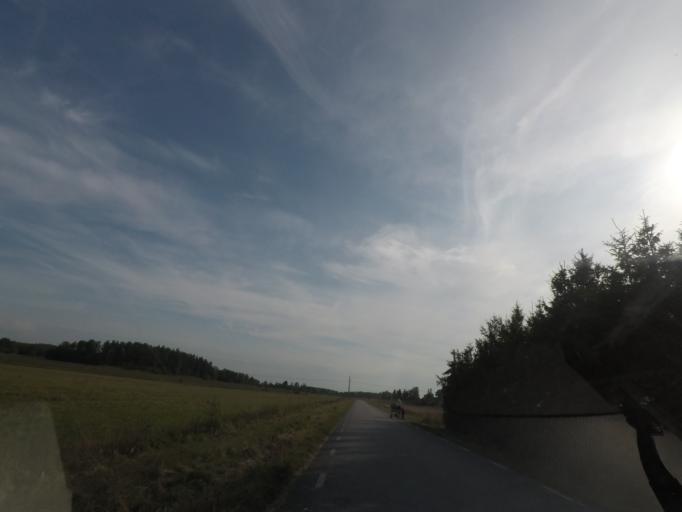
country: SE
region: Vaestmanland
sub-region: Hallstahammars Kommun
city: Kolback
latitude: 59.5321
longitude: 16.1413
